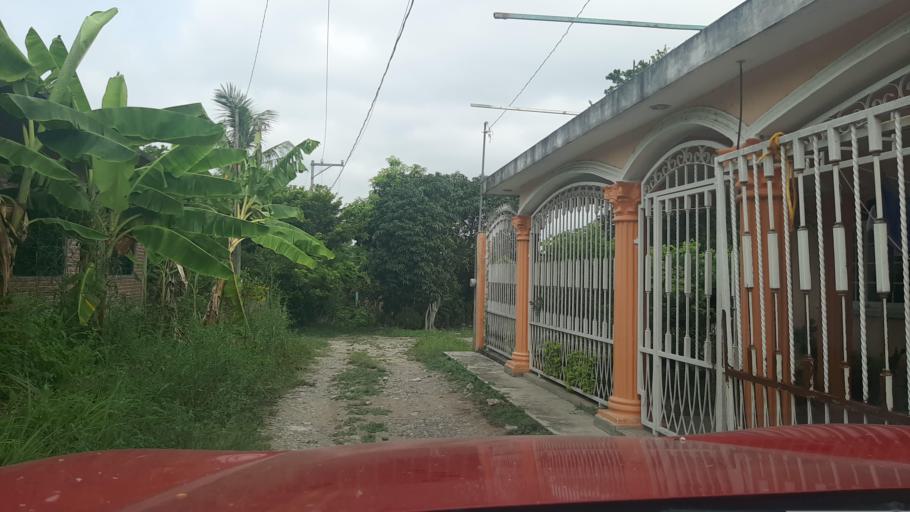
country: MX
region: Veracruz
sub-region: Coatzintla
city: Corralillos
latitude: 20.4842
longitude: -97.5044
